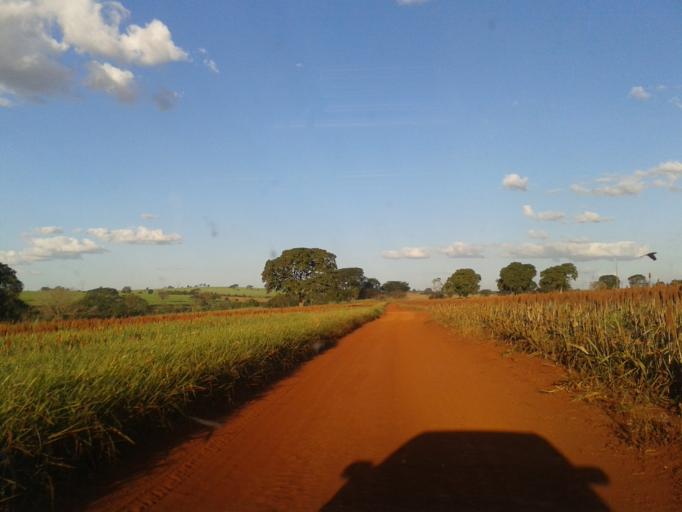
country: BR
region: Minas Gerais
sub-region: Centralina
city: Centralina
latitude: -18.6074
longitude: -49.3068
